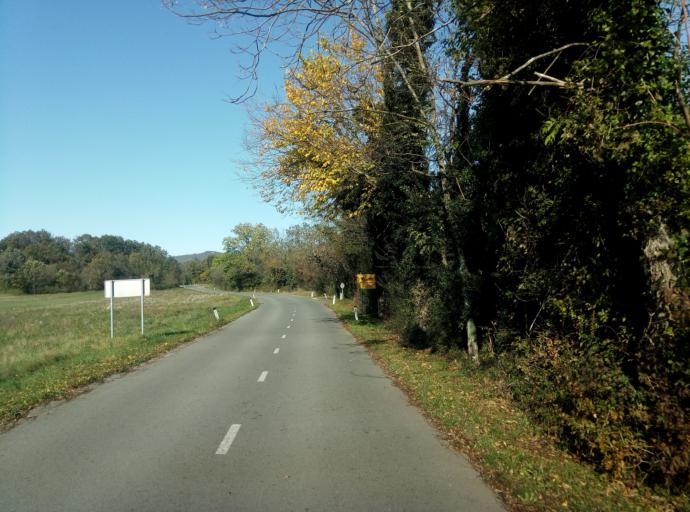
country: SI
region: Komen
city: Komen
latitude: 45.8219
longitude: 13.7466
